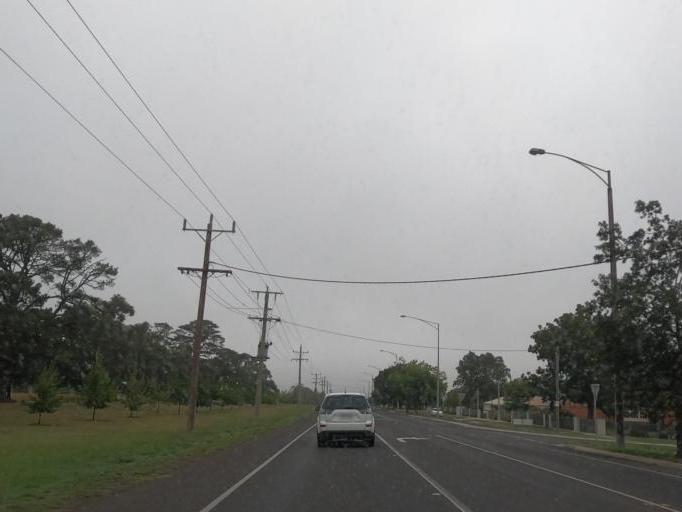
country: AU
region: Victoria
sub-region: Ballarat North
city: Newington
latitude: -37.5625
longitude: 143.8175
